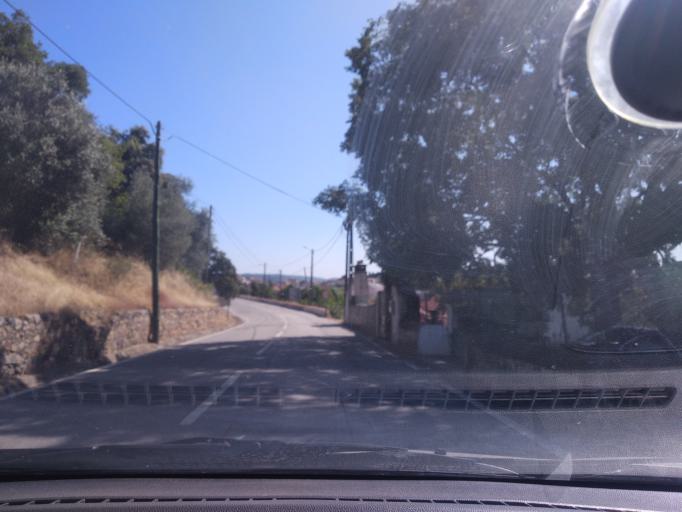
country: PT
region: Portalegre
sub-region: Nisa
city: Nisa
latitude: 39.6497
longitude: -7.6746
